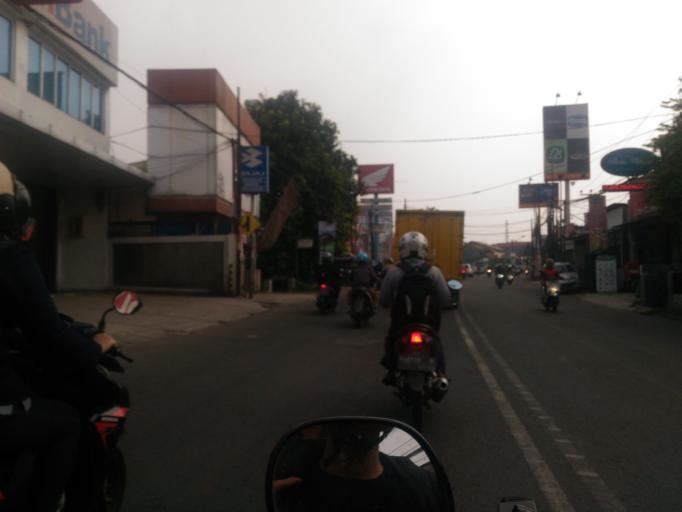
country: ID
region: West Java
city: Bogor
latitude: -6.5592
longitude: 106.8142
